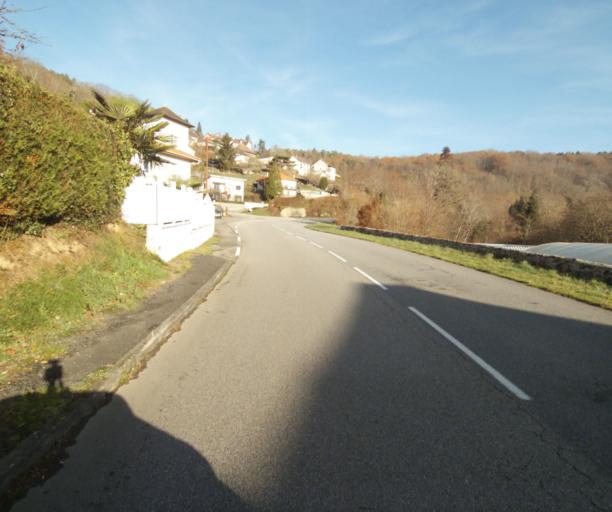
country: FR
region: Limousin
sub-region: Departement de la Correze
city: Laguenne
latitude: 45.2494
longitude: 1.7842
